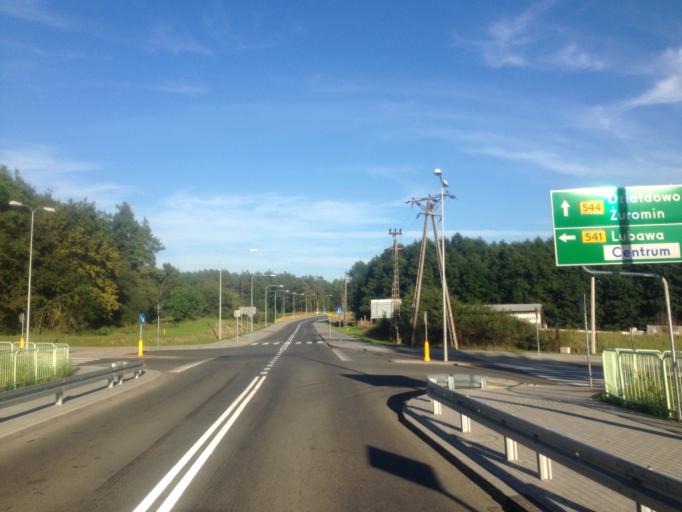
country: PL
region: Warmian-Masurian Voivodeship
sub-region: Powiat dzialdowski
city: Lidzbark
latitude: 53.2684
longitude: 19.8193
